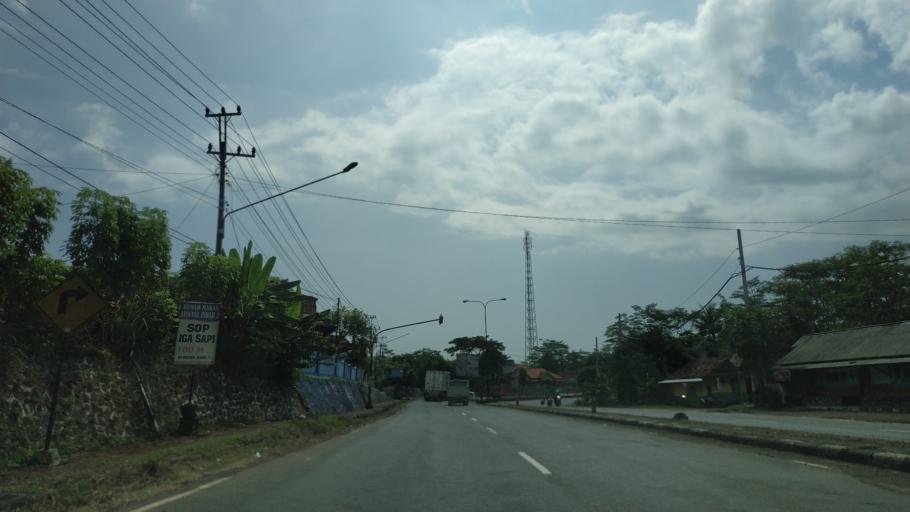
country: ID
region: Central Java
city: Pekalongan
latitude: -6.9456
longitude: 109.8181
